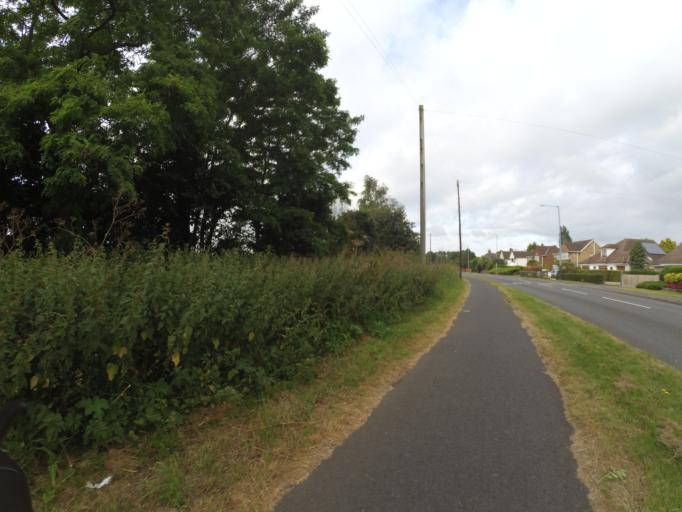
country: GB
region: England
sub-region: Warwickshire
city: Rugby
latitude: 52.3563
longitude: -1.2390
